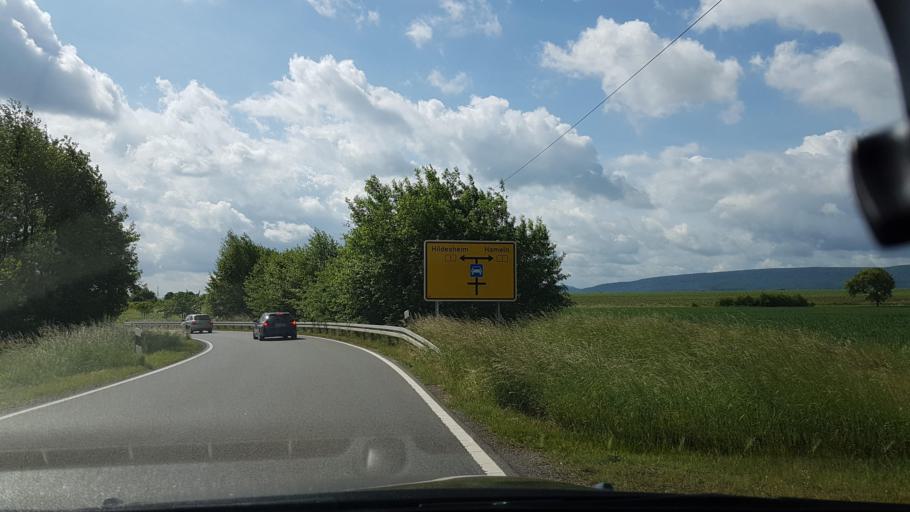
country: DE
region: Lower Saxony
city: Elze
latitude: 52.1168
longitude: 9.6820
